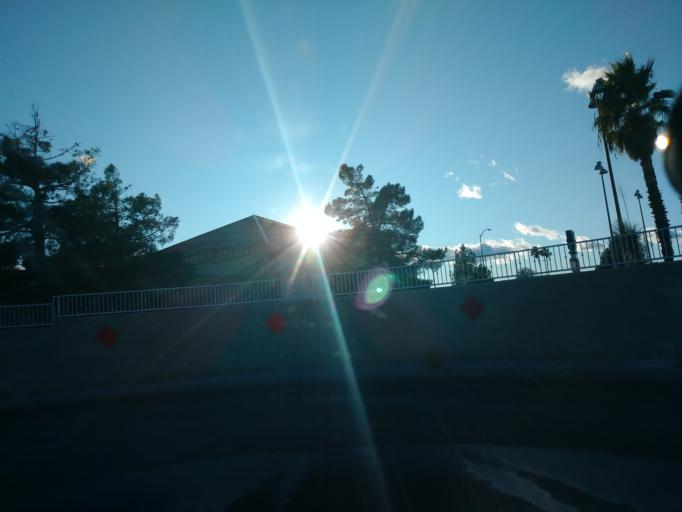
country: US
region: Nevada
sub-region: Clark County
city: Spring Valley
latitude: 36.1480
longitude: -115.2422
